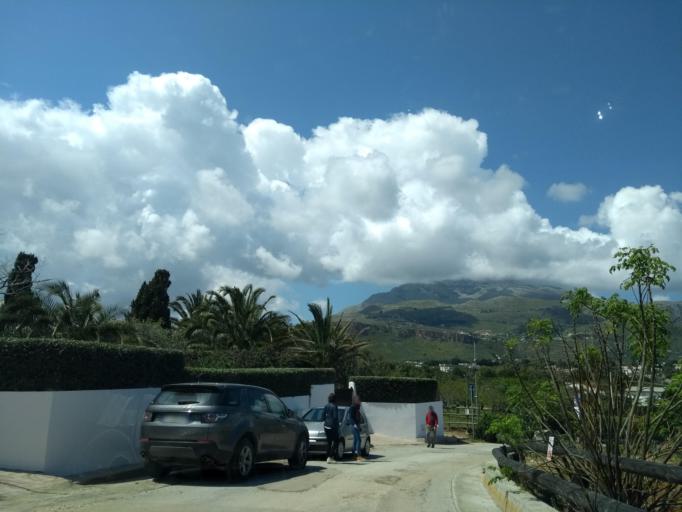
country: IT
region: Sicily
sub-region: Trapani
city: Castellammare del Golfo
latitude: 38.0547
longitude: 12.8441
